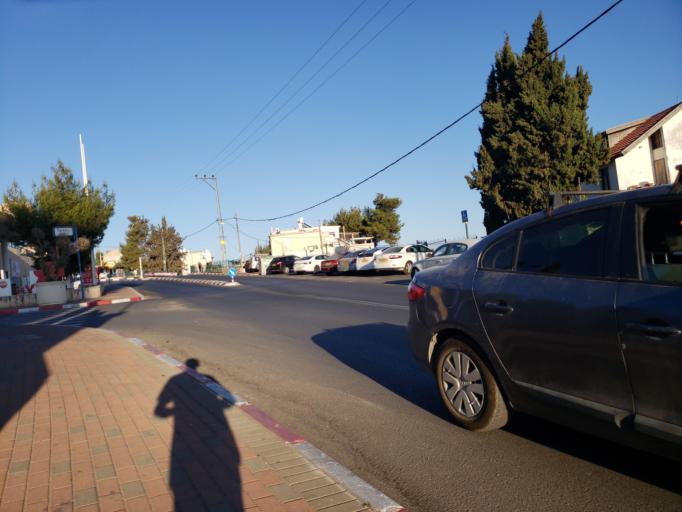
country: IL
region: Northern District
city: Safed
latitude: 32.9573
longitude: 35.4969
